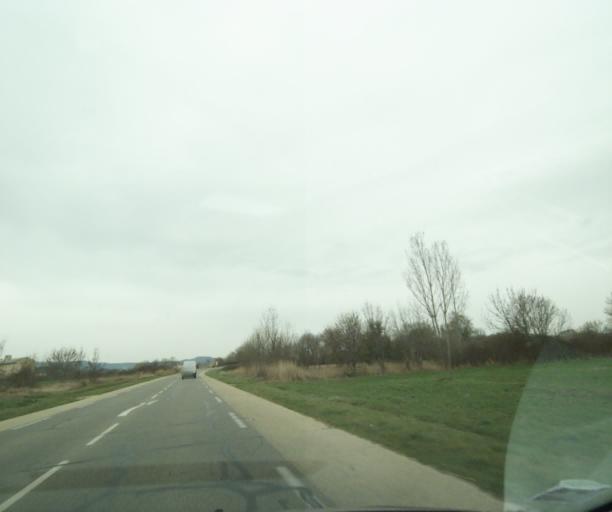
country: FR
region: Provence-Alpes-Cote d'Azur
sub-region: Departement des Bouches-du-Rhone
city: Meyrargues
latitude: 43.6476
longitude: 5.5509
